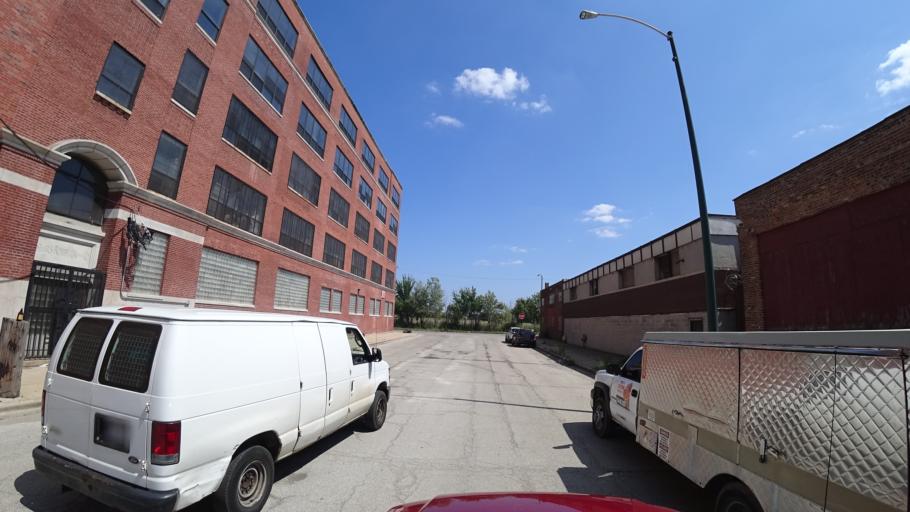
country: US
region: Illinois
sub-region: Cook County
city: Cicero
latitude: 41.8678
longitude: -87.7358
